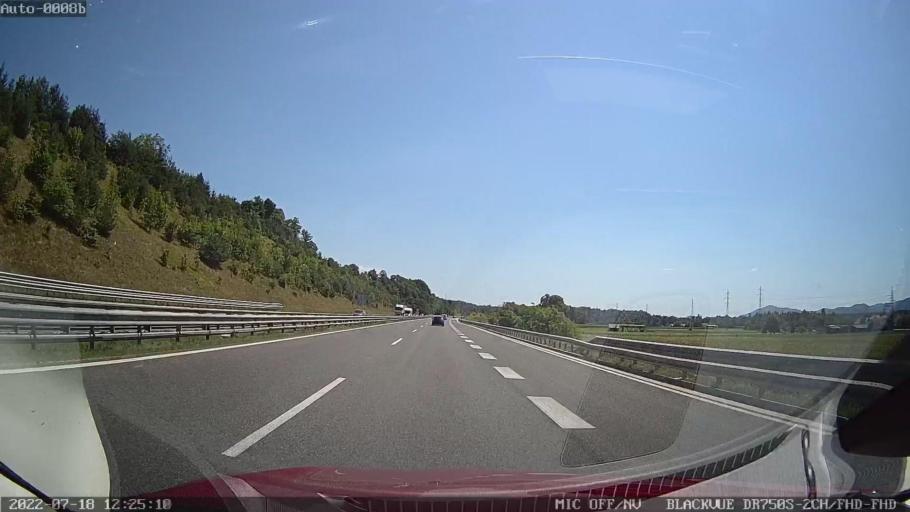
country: SI
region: Radovljica
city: Radovljica
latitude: 46.3266
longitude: 14.2221
